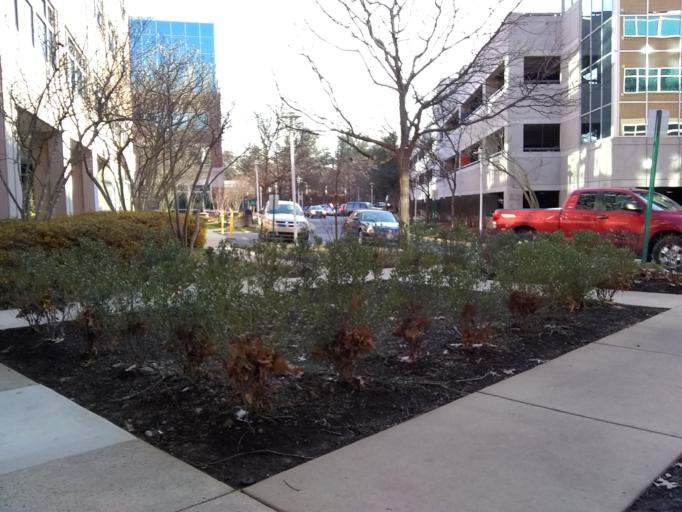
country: US
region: Virginia
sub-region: Fairfax County
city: Merrifield
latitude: 38.8646
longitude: -77.2396
